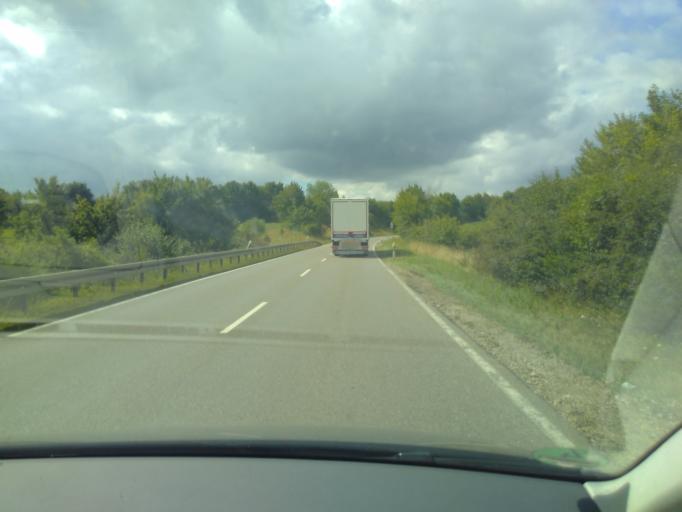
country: DE
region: Baden-Wuerttemberg
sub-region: Tuebingen Region
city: Merklingen
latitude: 48.4957
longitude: 9.7333
